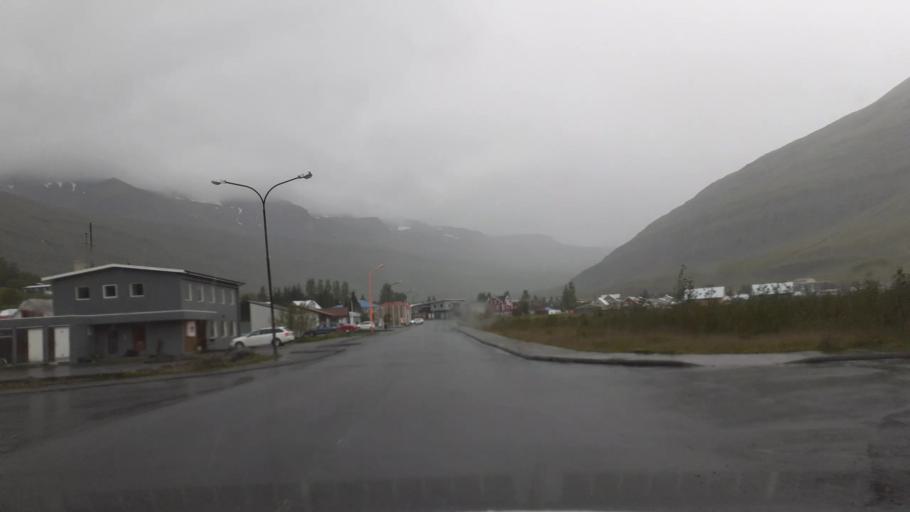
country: IS
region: East
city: Eskifjoerdur
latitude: 65.2632
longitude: -13.9971
